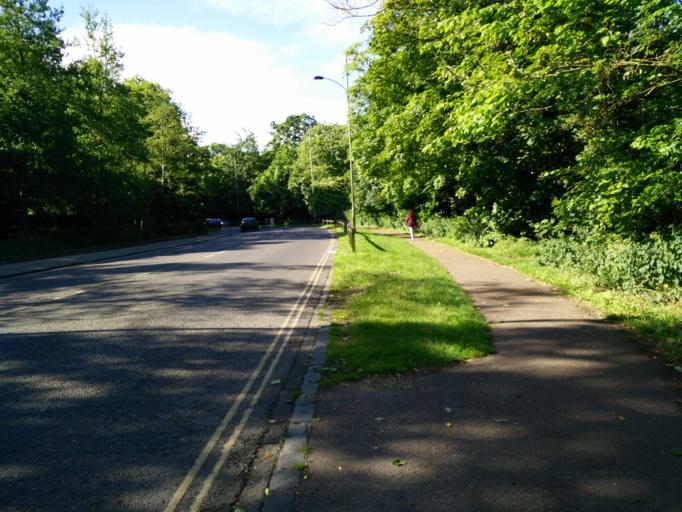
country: GB
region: England
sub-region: Cambridgeshire
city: Cambridge
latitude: 52.2081
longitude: 0.1108
